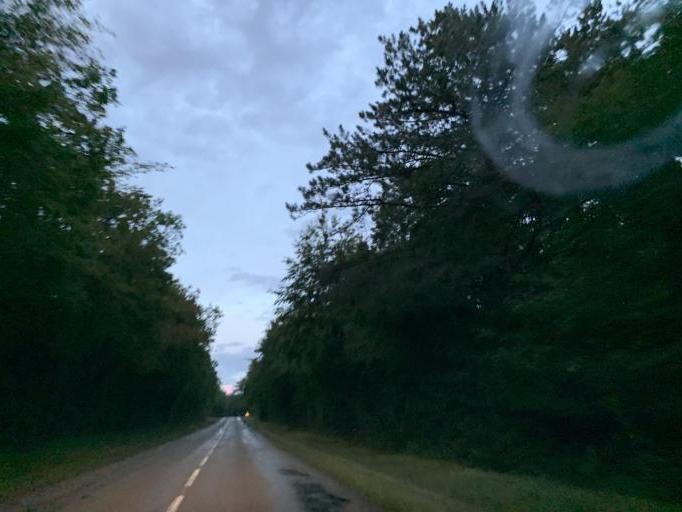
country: FR
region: Bourgogne
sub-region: Departement de l'Yonne
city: Fontenailles
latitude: 47.5687
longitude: 3.4495
